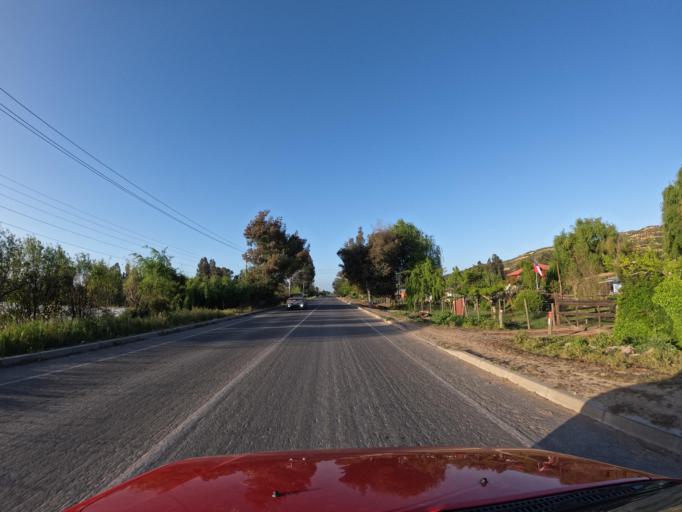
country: CL
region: O'Higgins
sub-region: Provincia de Colchagua
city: Santa Cruz
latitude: -34.3462
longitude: -71.4062
